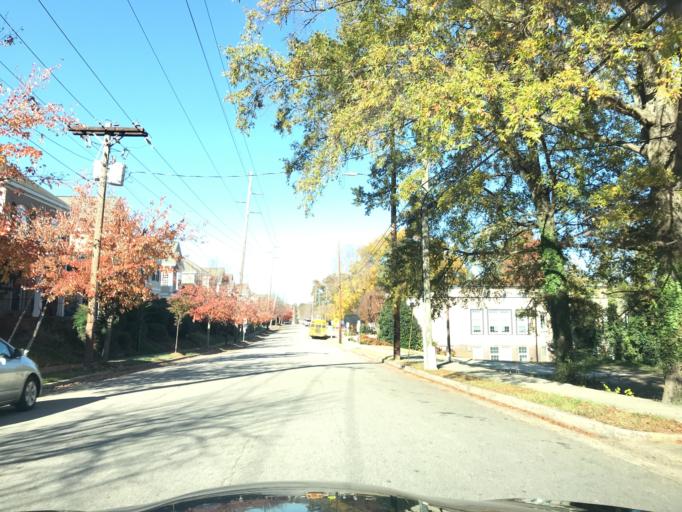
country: US
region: North Carolina
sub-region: Wake County
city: Raleigh
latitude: 35.7944
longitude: -78.6356
